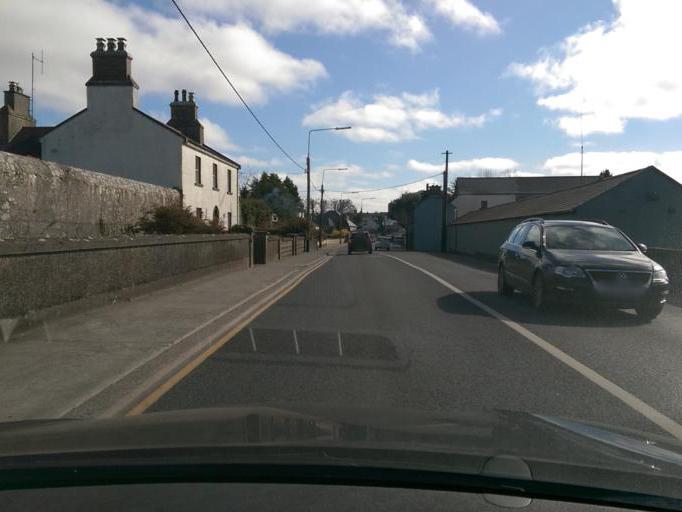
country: IE
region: Connaught
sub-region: County Galway
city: Ballinasloe
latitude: 53.3299
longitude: -8.2134
